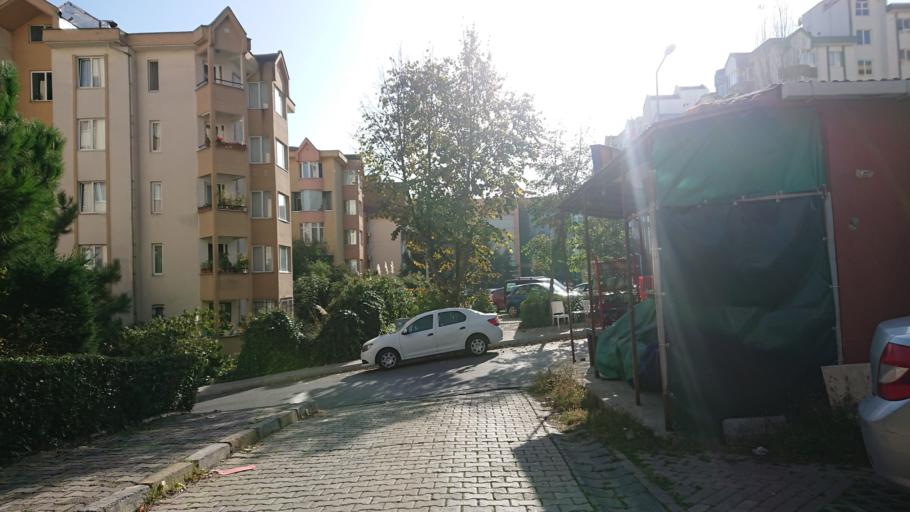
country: TR
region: Istanbul
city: Esenyurt
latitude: 41.0624
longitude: 28.6770
